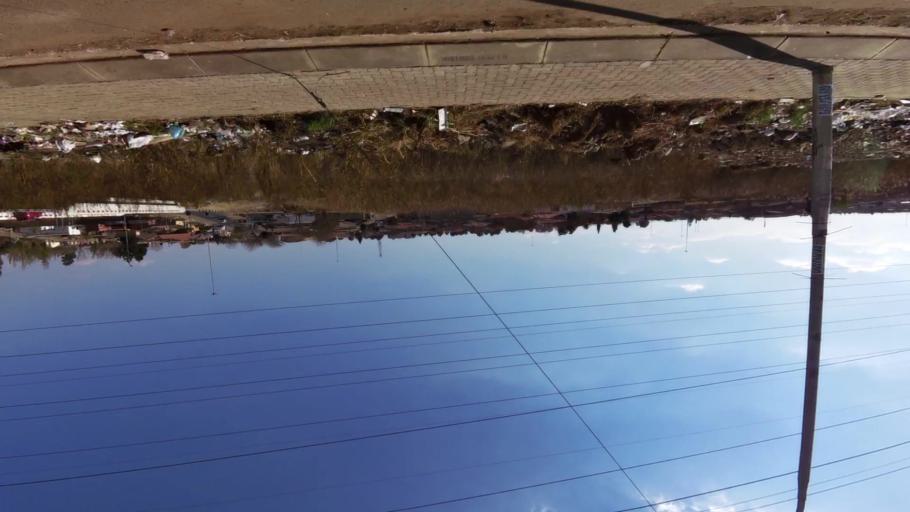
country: ZA
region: Gauteng
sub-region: City of Johannesburg Metropolitan Municipality
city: Soweto
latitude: -26.2392
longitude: 27.8879
